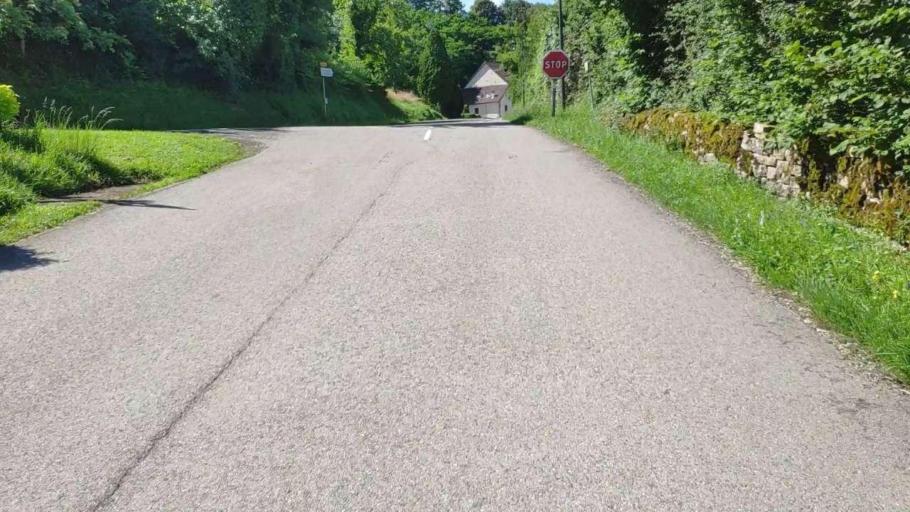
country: FR
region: Franche-Comte
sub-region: Departement du Jura
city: Bletterans
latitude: 46.7994
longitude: 5.5619
